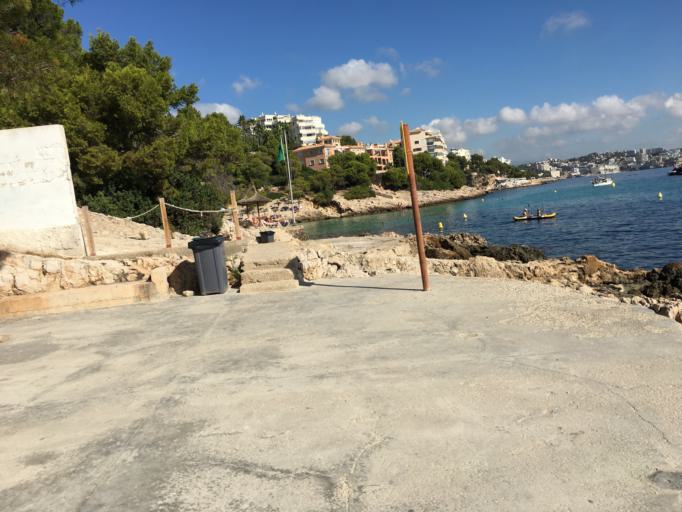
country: ES
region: Balearic Islands
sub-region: Illes Balears
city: Magaluf
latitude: 39.5338
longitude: 2.5896
